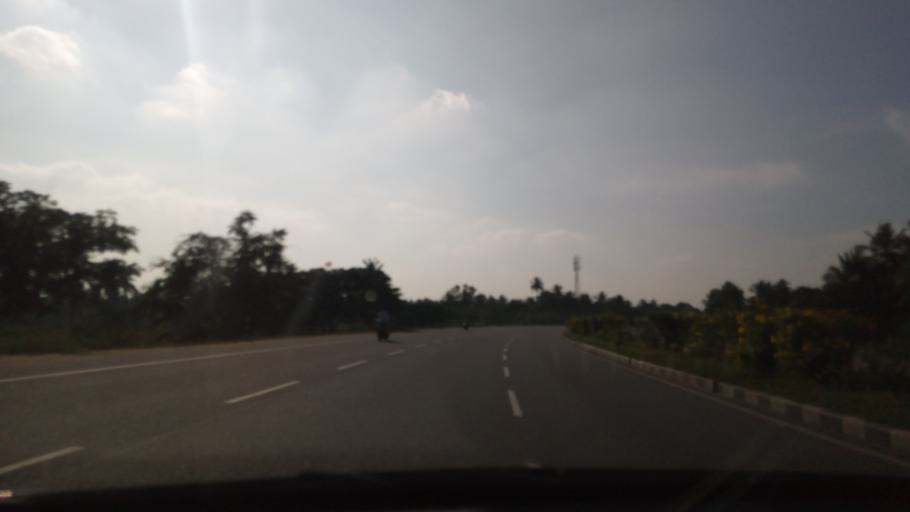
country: IN
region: Tamil Nadu
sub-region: Krishnagiri
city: Krishnagiri
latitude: 12.5333
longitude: 78.2903
